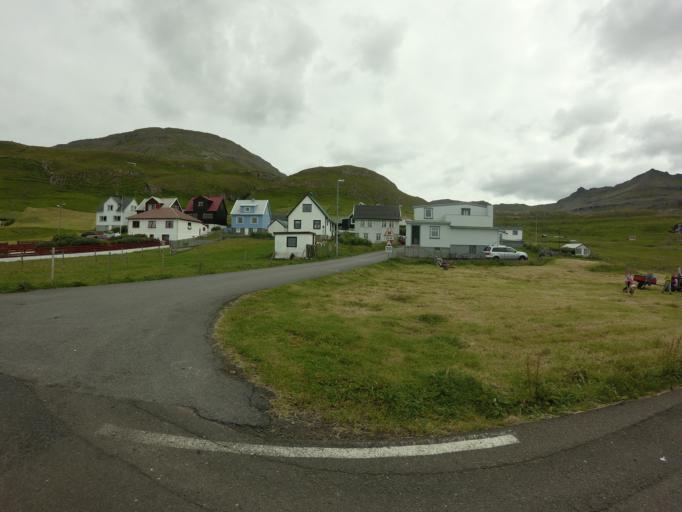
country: FO
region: Suduroy
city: Tvoroyri
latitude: 61.5239
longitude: -6.8794
